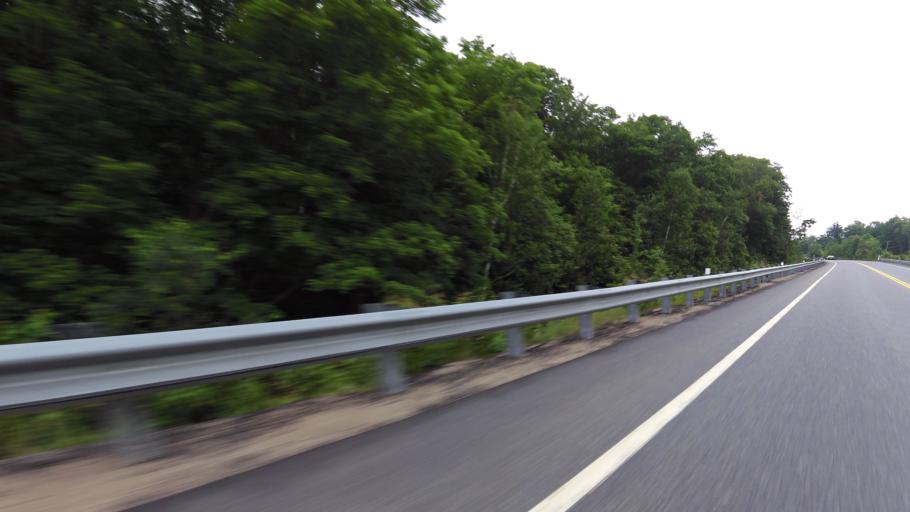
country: CA
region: Ontario
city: Huntsville
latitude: 45.4239
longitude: -78.8403
